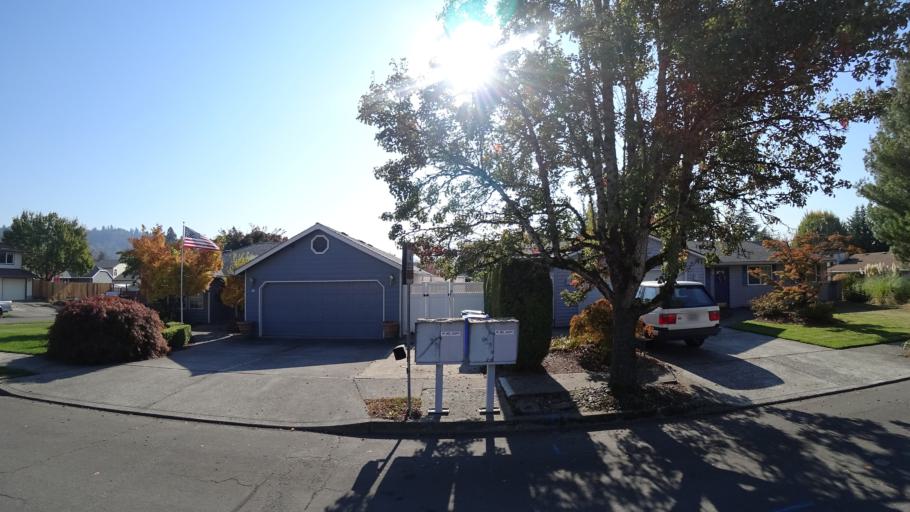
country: US
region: Oregon
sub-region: Multnomah County
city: Gresham
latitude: 45.4958
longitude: -122.4535
